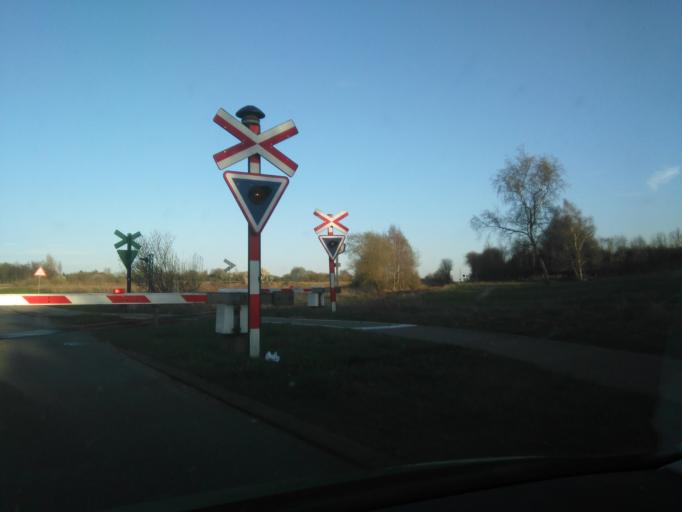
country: DK
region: Central Jutland
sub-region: Arhus Kommune
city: Tranbjerg
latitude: 56.1079
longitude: 10.1255
